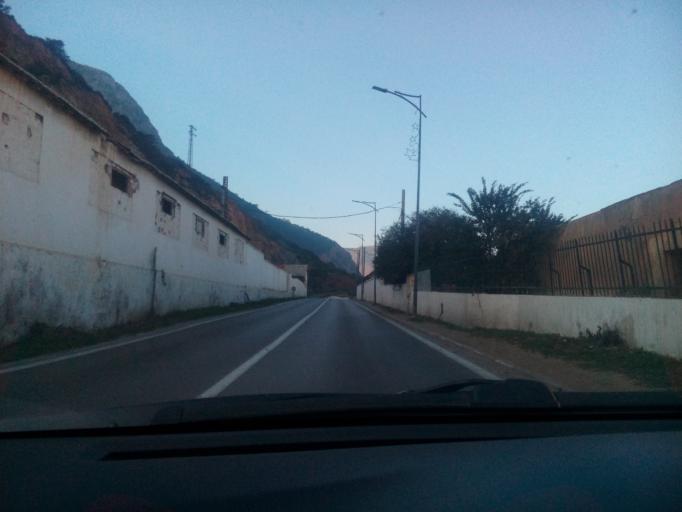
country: DZ
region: Oran
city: Oran
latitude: 35.7141
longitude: -0.6645
